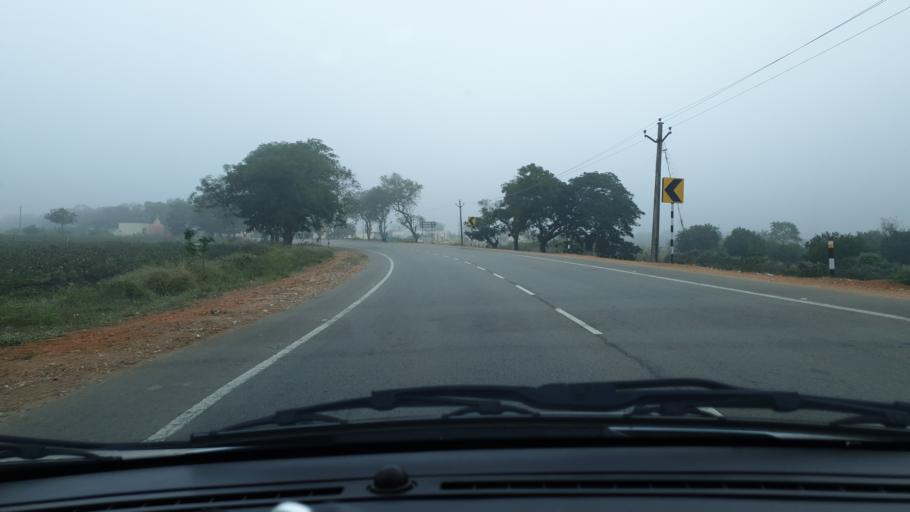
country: IN
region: Telangana
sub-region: Nalgonda
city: Devarkonda
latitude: 16.6304
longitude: 78.6104
